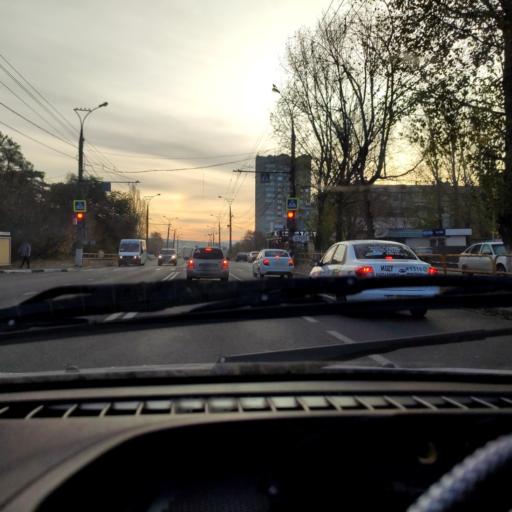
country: RU
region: Samara
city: Zhigulevsk
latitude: 53.4872
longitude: 49.4689
